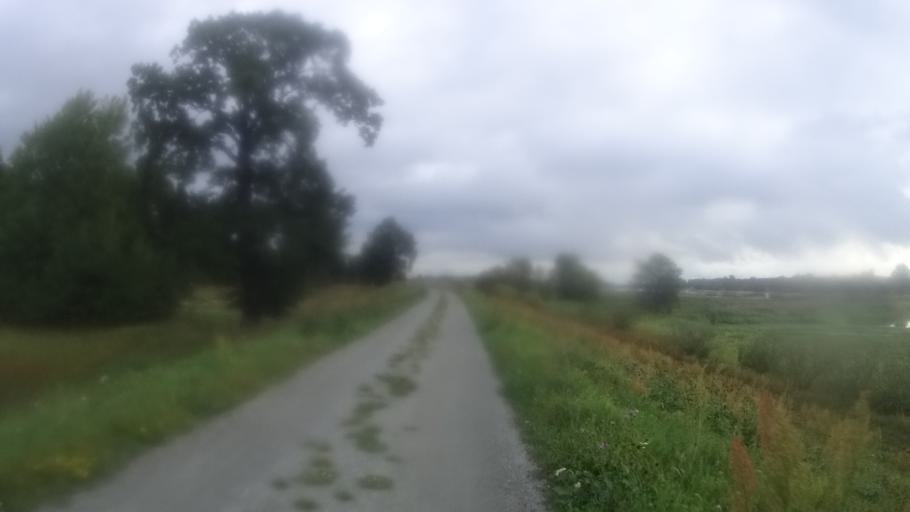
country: DE
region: Lower Saxony
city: Gorleben
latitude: 53.0658
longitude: 11.3802
